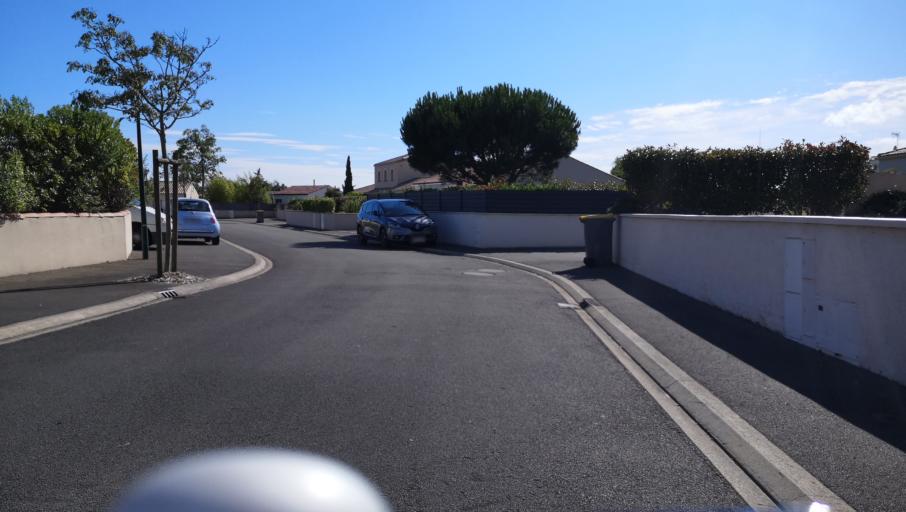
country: FR
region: Pays de la Loire
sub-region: Departement de la Vendee
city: Les Sables-d'Olonne
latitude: 46.5131
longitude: -1.7861
